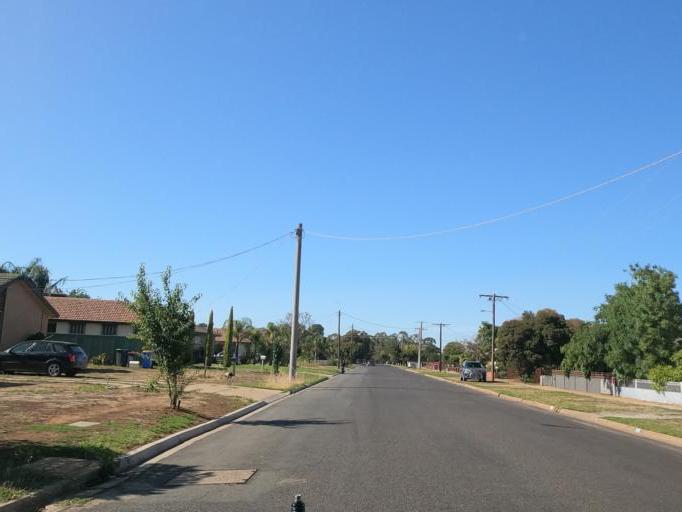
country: AU
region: Victoria
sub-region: Moira
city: Yarrawonga
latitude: -36.0225
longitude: 146.0054
